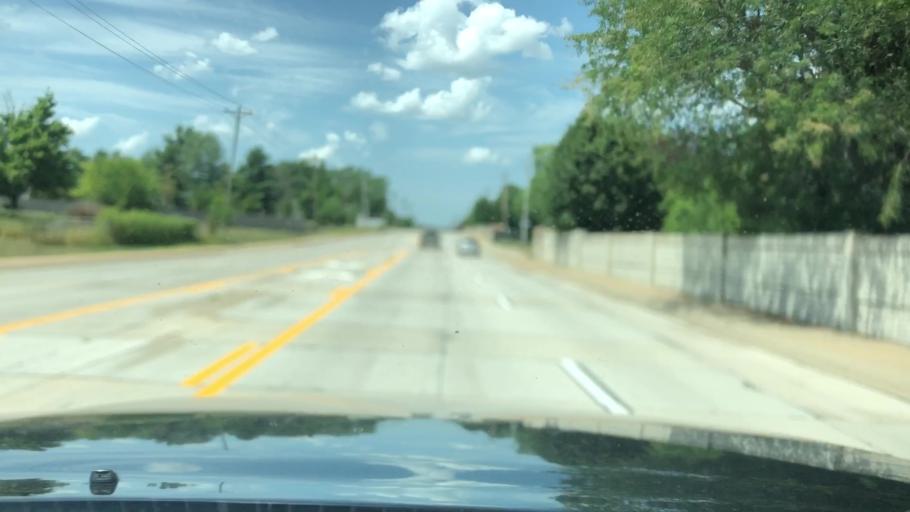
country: US
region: Missouri
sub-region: Saint Charles County
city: Saint Peters
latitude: 38.7869
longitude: -90.6499
